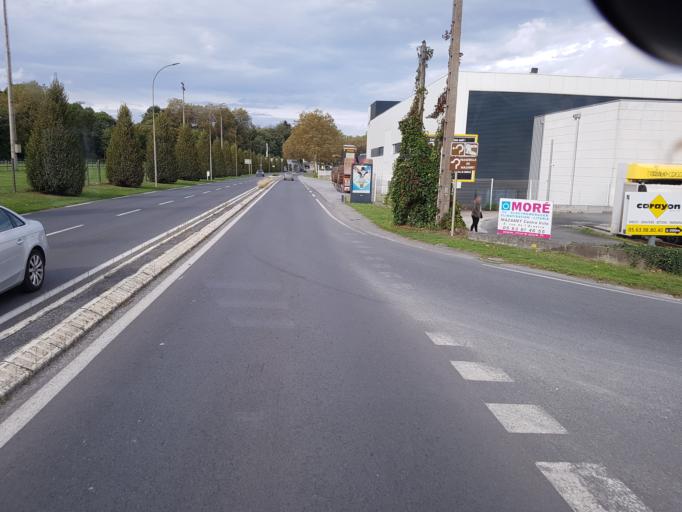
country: FR
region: Midi-Pyrenees
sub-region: Departement du Tarn
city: Pont-de-Larn
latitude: 43.4981
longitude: 2.3907
